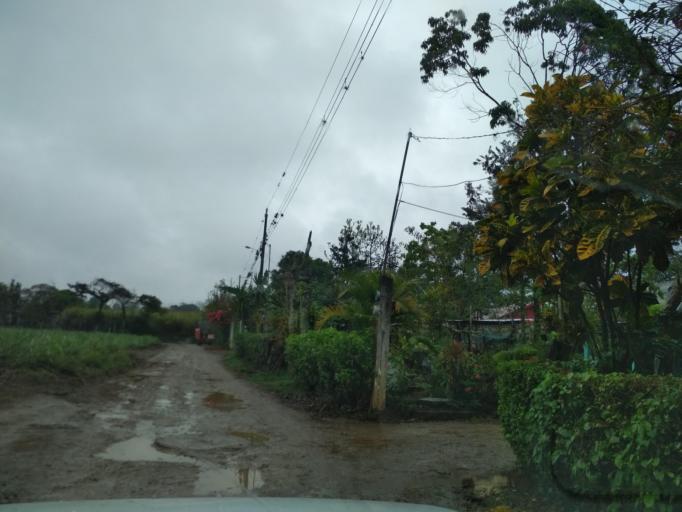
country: MX
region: Veracruz
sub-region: Amatlan de los Reyes
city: Centro de Readaptacion Social
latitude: 18.8344
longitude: -96.9320
